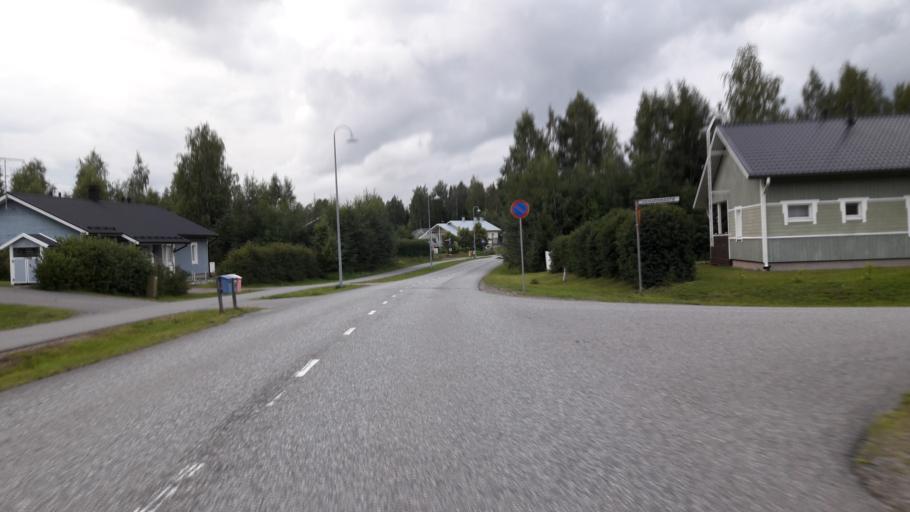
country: FI
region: North Karelia
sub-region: Joensuu
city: Joensuu
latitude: 62.5229
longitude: 29.8461
